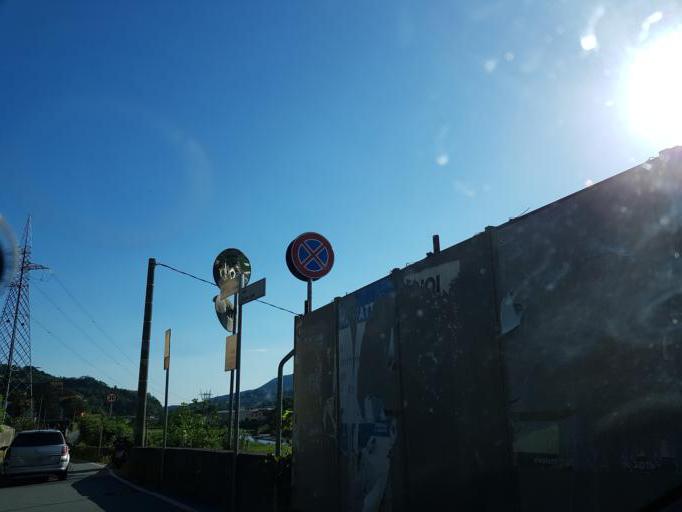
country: IT
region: Liguria
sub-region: Provincia di Genova
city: Manesseno
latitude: 44.4809
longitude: 8.9210
